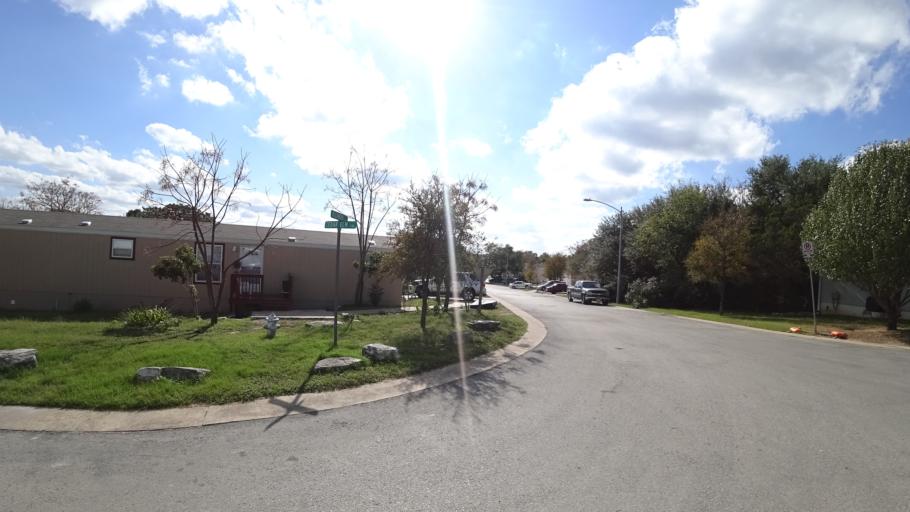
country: US
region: Texas
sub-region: Travis County
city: Barton Creek
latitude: 30.2507
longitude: -97.8839
